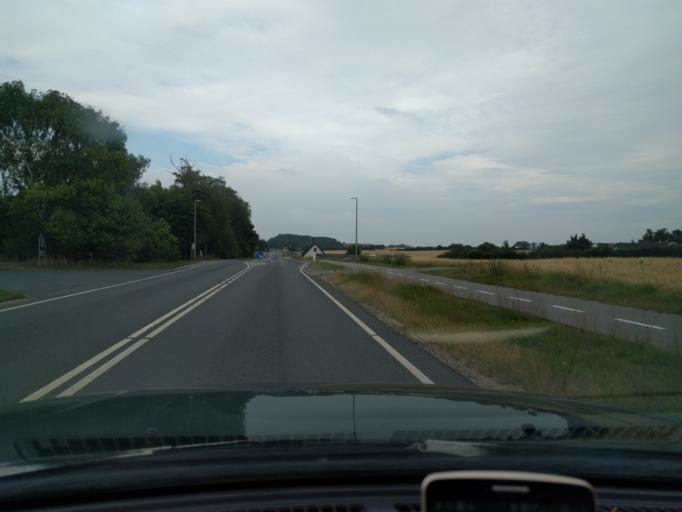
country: DK
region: Zealand
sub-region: Slagelse Kommune
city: Skaelskor
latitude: 55.3115
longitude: 11.2302
